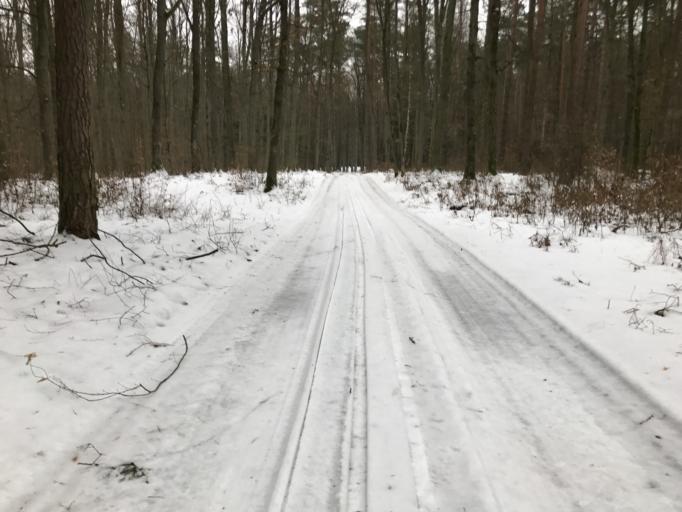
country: PL
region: Kujawsko-Pomorskie
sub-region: Powiat brodnicki
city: Gorzno
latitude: 53.1839
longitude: 19.6911
